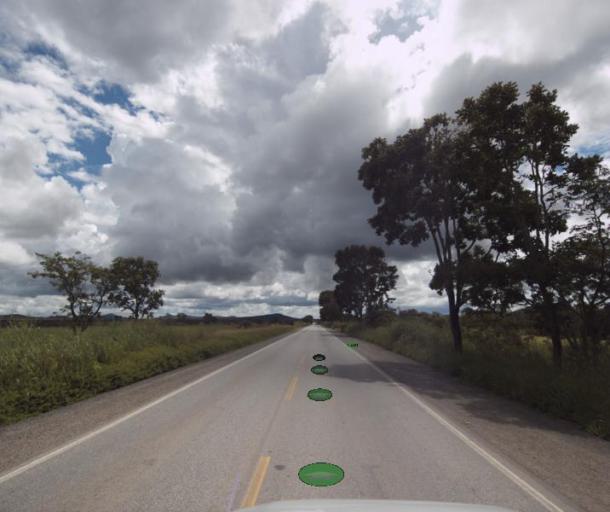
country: BR
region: Goias
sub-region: Uruacu
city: Uruacu
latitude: -14.2770
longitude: -49.1471
